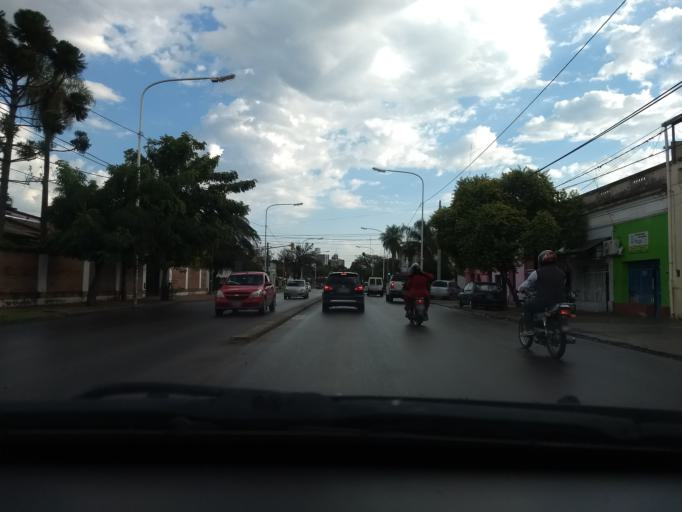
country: AR
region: Corrientes
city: Corrientes
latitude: -27.4797
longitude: -58.8284
